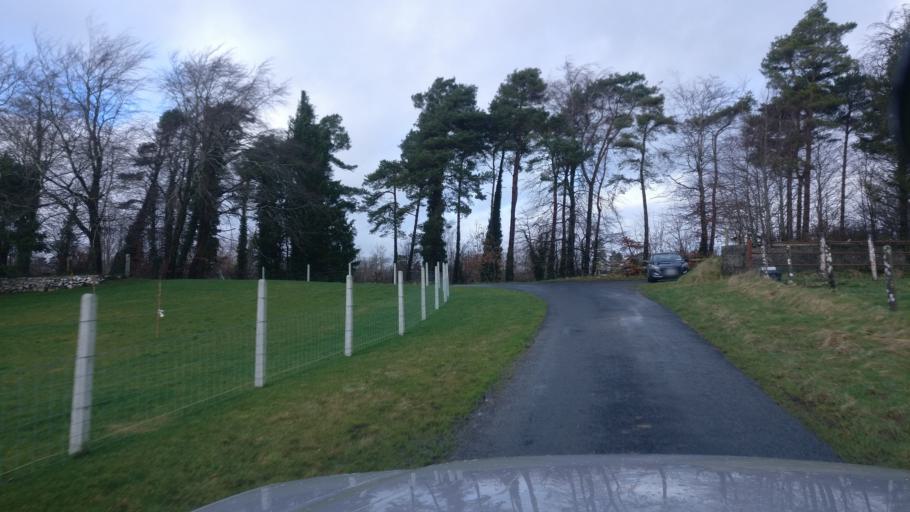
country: IE
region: Connaught
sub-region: County Galway
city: Loughrea
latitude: 53.2426
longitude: -8.6516
